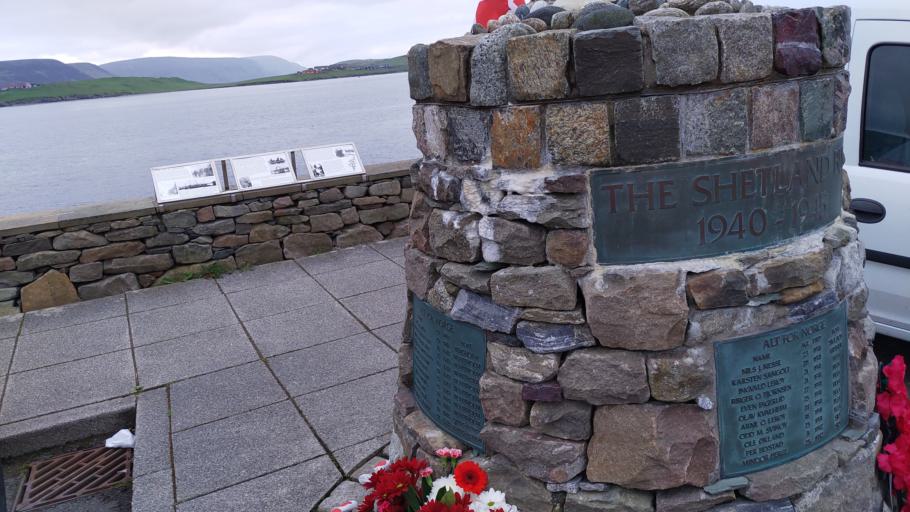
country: GB
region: Scotland
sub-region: Shetland Islands
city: Lerwick
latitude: 60.1375
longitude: -1.2795
